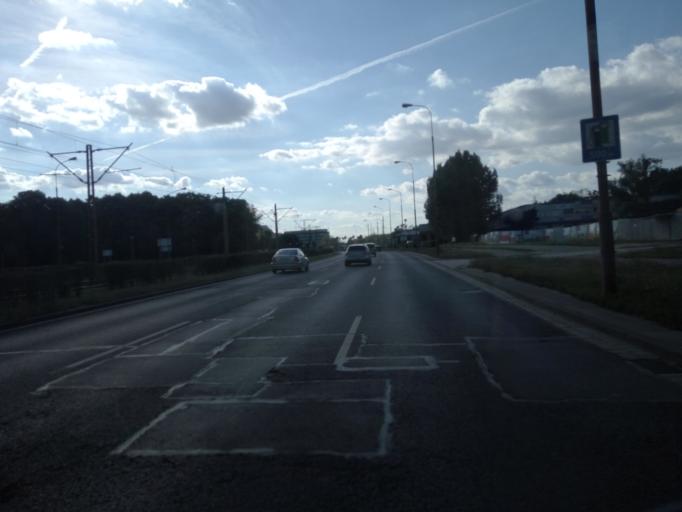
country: PL
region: Lower Silesian Voivodeship
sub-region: Powiat wroclawski
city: Wroclaw
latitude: 51.1242
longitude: 16.9873
